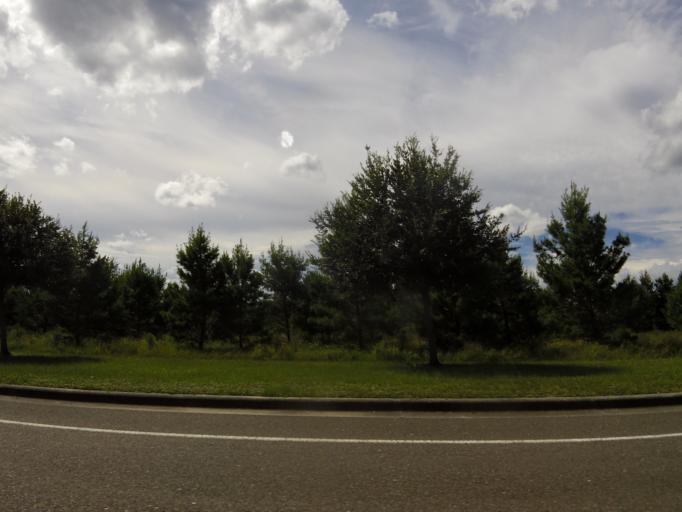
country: US
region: Florida
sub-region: Duval County
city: Jacksonville
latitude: 30.4151
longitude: -81.6425
